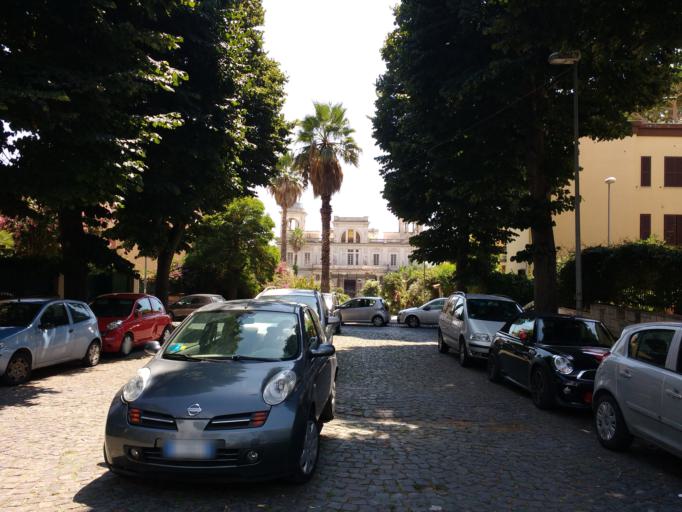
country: IT
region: Latium
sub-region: Citta metropolitana di Roma Capitale
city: Anzio
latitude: 41.4528
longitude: 12.6339
